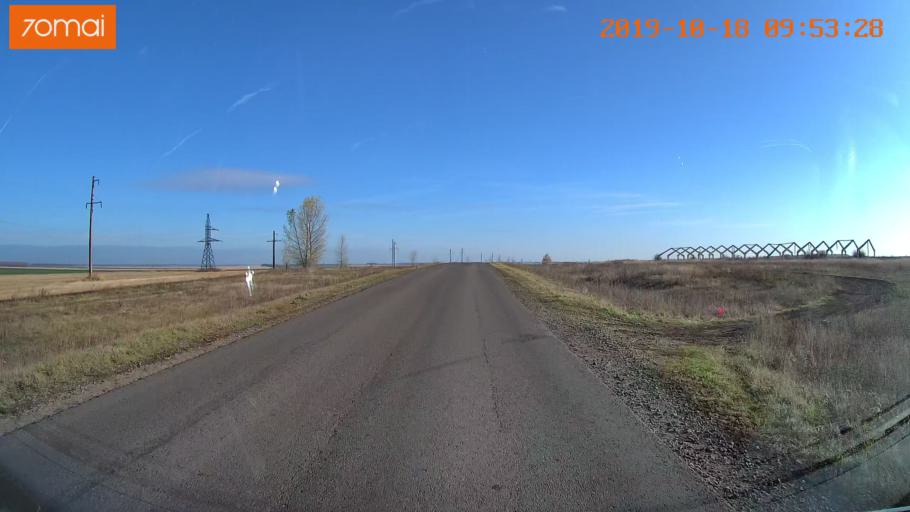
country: RU
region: Tula
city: Kazachka
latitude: 53.3612
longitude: 38.3297
